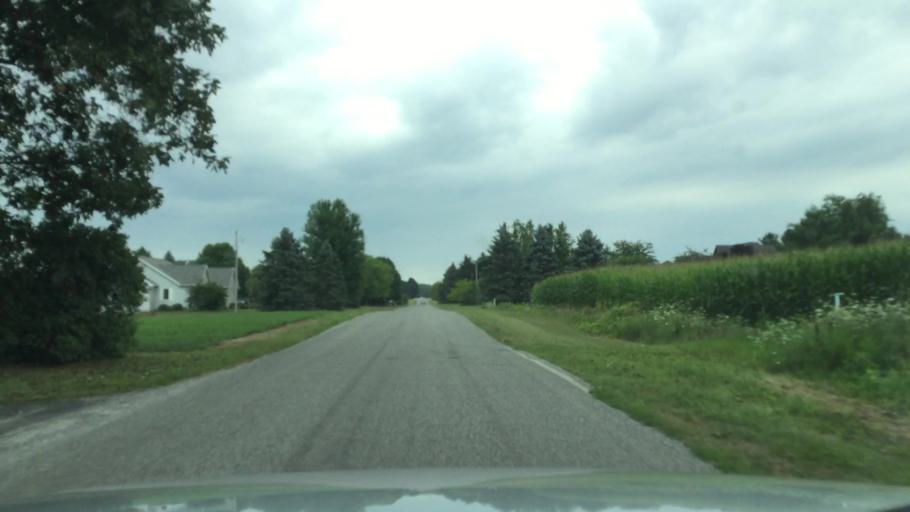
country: US
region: Michigan
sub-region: Saginaw County
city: Frankenmuth
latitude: 43.3145
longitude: -83.7956
